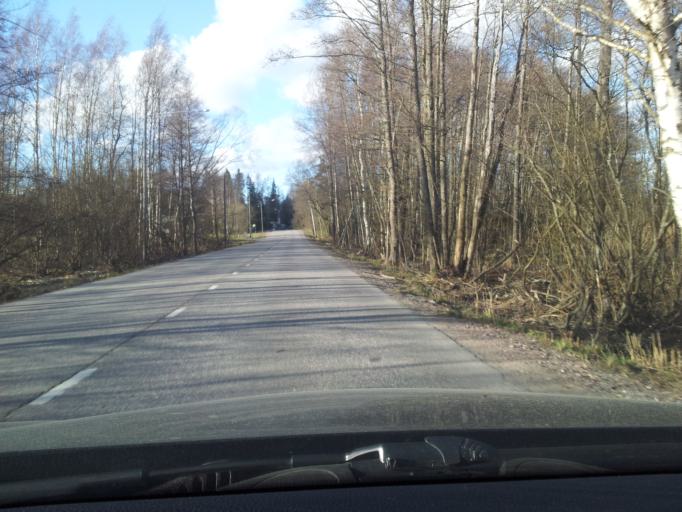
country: FI
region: Uusimaa
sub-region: Helsinki
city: Espoo
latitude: 60.1363
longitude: 24.6821
